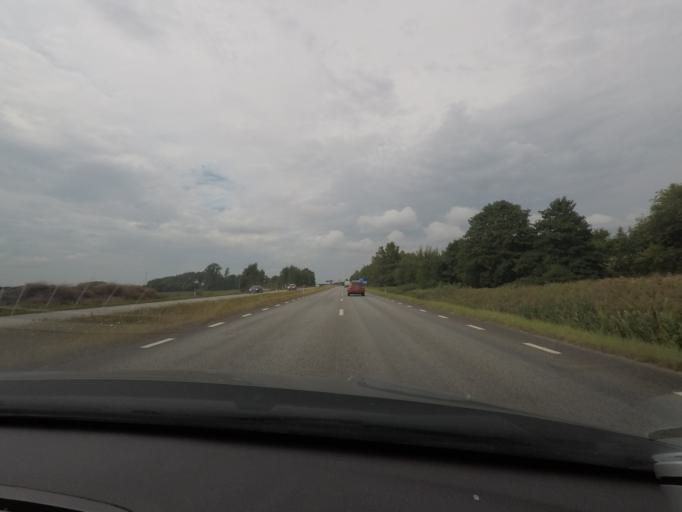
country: SE
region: Halland
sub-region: Halmstads Kommun
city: Fyllinge
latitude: 56.6463
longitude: 12.9185
